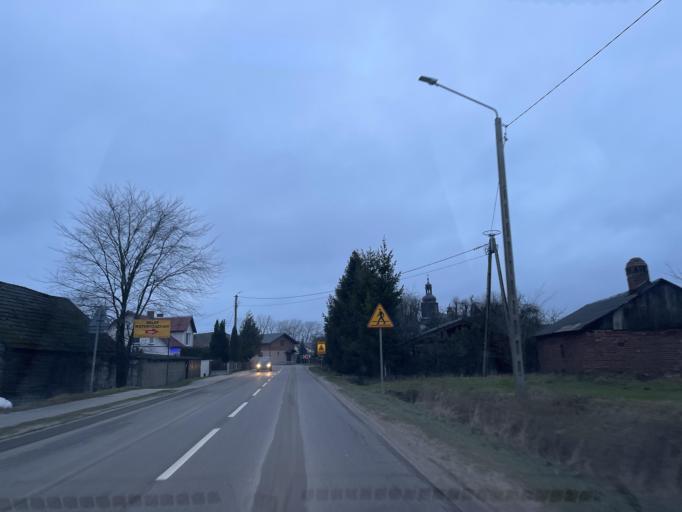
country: PL
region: Pomeranian Voivodeship
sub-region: Powiat wejherowski
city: Szemud
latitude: 54.4140
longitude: 18.2029
